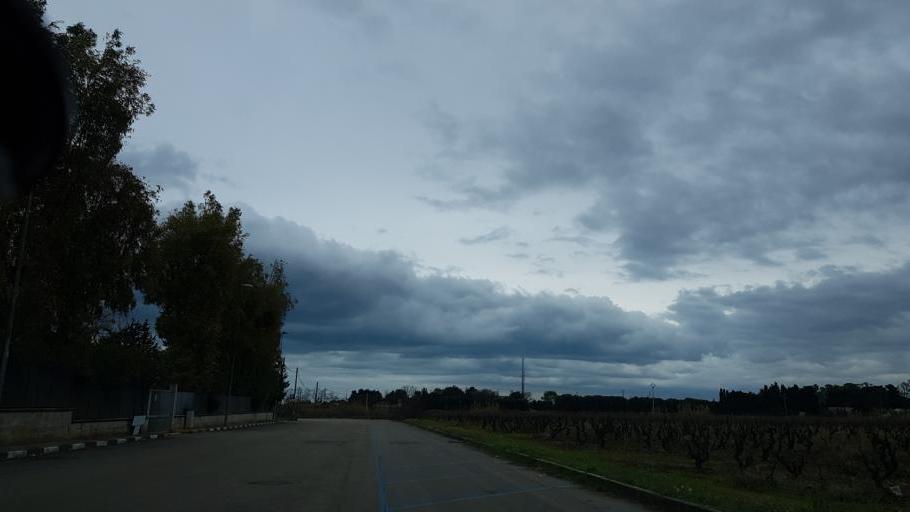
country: IT
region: Apulia
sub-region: Provincia di Brindisi
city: La Rosa
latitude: 40.6133
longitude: 17.9486
